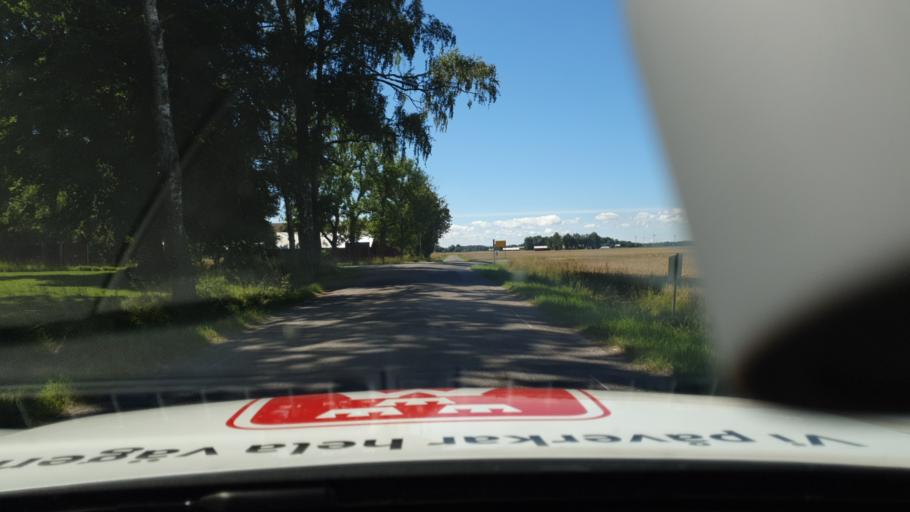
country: SE
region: Vaestra Goetaland
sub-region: Lidkopings Kommun
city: Vinninga
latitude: 58.3820
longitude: 13.2774
